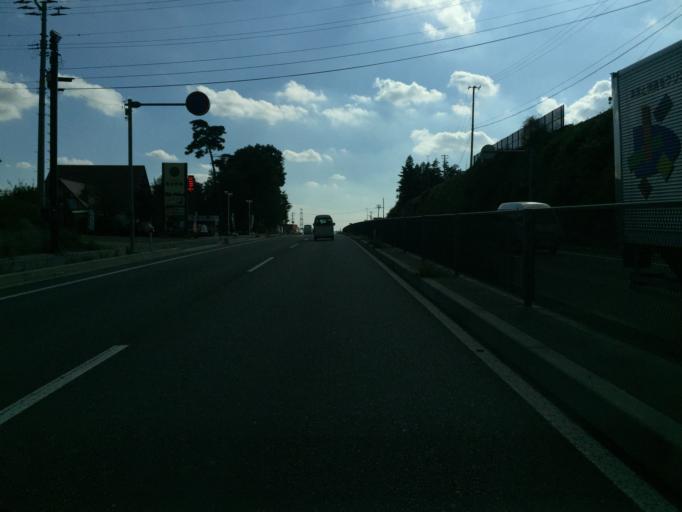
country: JP
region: Fukushima
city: Motomiya
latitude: 37.5518
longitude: 140.4015
